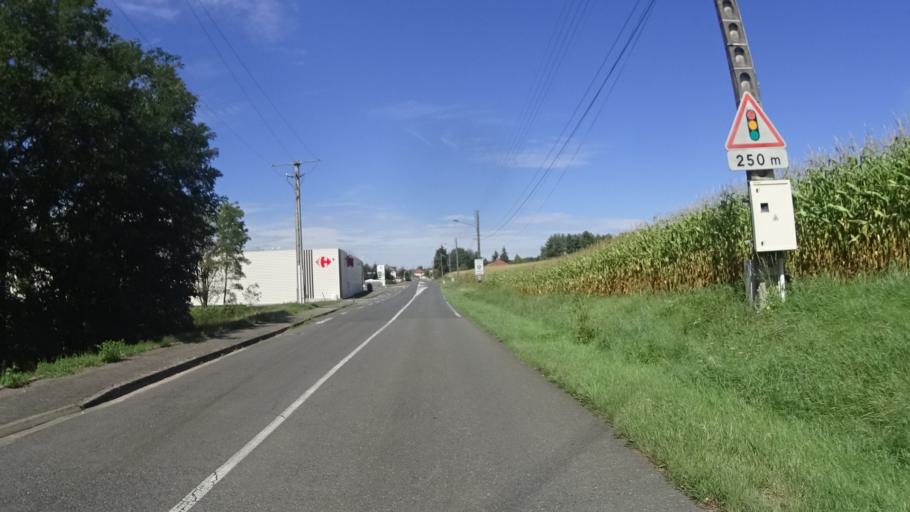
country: FR
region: Centre
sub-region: Departement du Loiret
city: Briare
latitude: 47.6239
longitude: 2.7512
